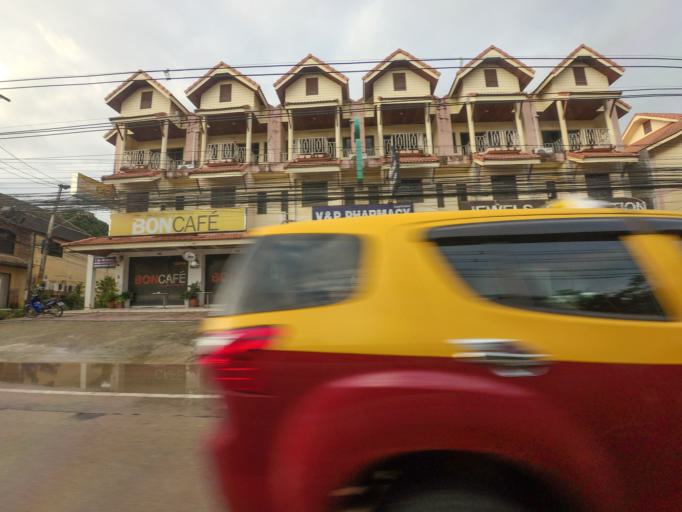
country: TH
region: Surat Thani
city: Ko Samui
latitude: 9.5590
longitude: 100.0259
